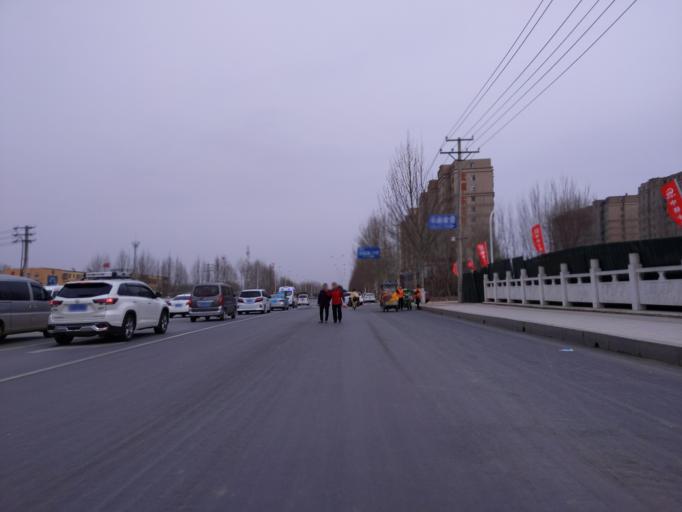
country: CN
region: Henan Sheng
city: Zhongyuanlu
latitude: 35.7565
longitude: 115.0815
